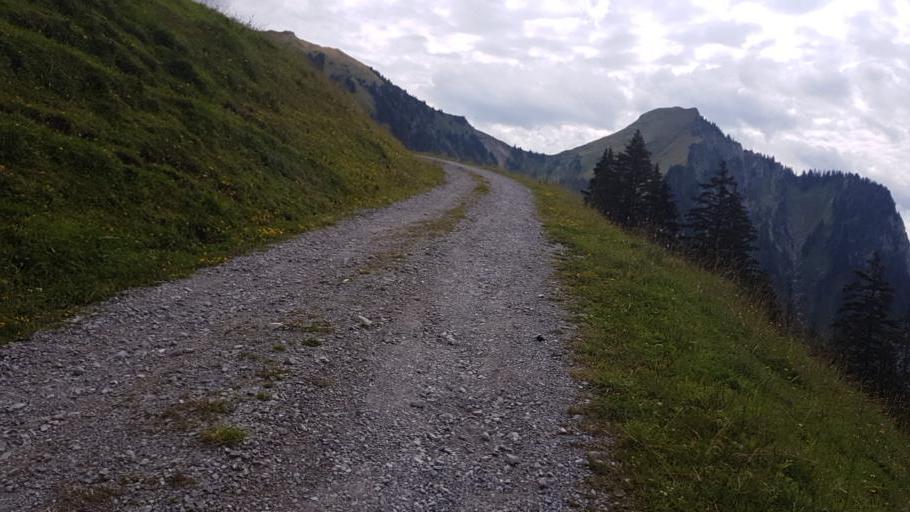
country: CH
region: Bern
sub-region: Obersimmental-Saanen District
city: Boltigen
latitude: 46.6920
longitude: 7.4382
